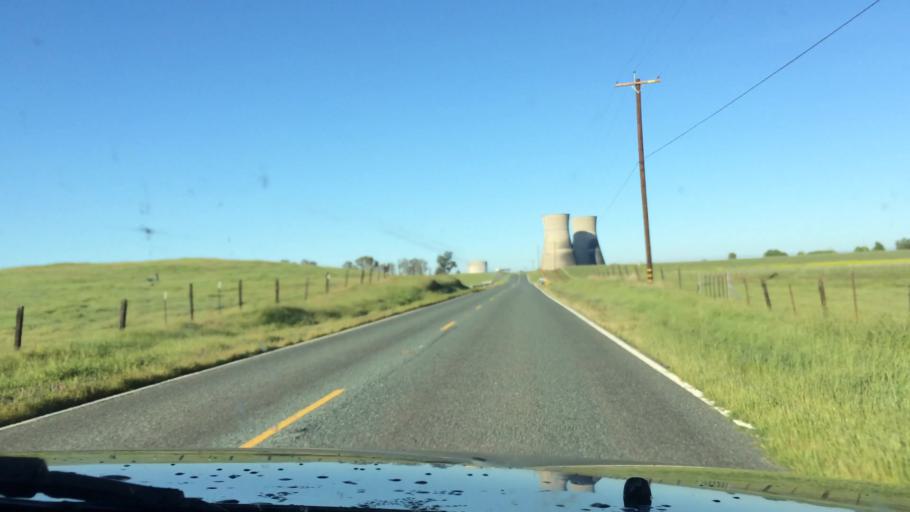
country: US
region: California
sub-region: Sacramento County
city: Clay
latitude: 38.3531
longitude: -121.1025
